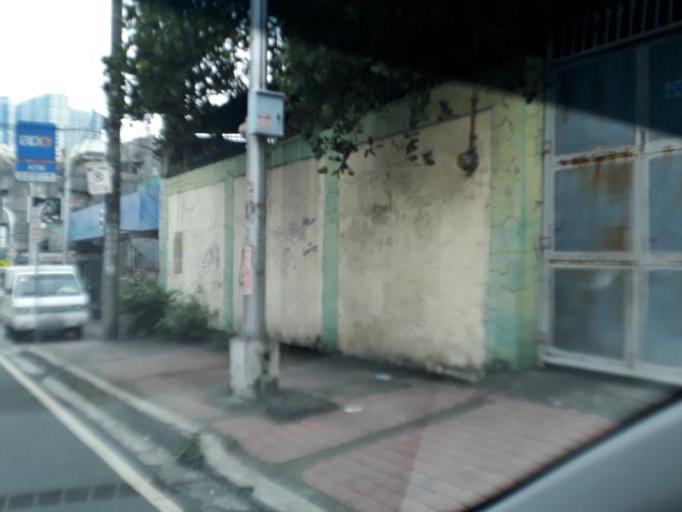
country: PH
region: Metro Manila
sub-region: City of Manila
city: Manila
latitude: 14.6238
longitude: 120.9988
